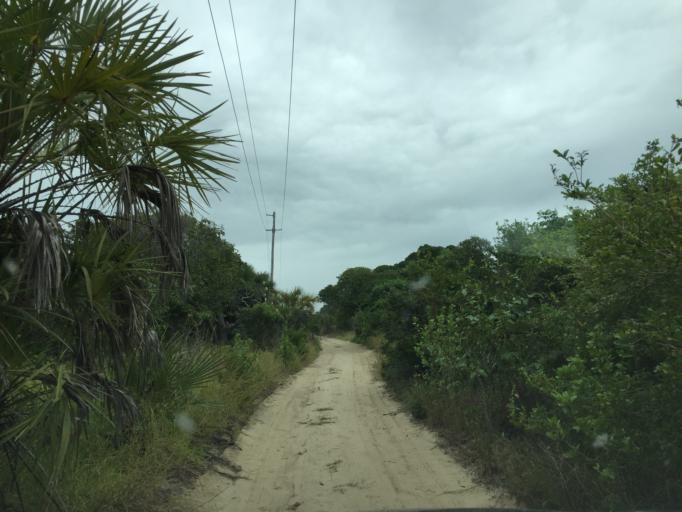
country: TZ
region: Pwani
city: Vikindu
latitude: -6.9406
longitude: 39.4908
